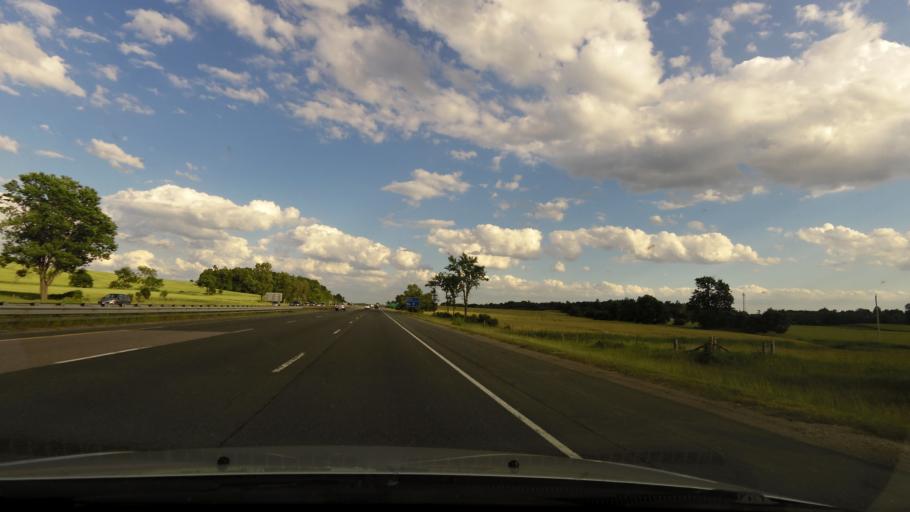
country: CA
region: Ontario
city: Bradford West Gwillimbury
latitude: 44.0615
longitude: -79.6174
